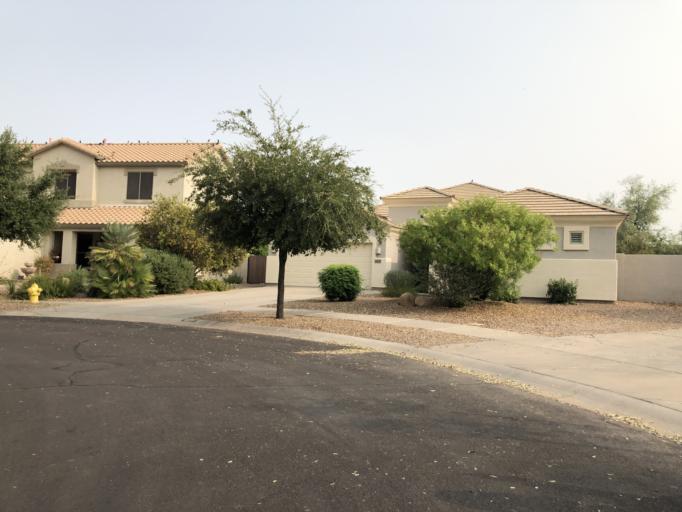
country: US
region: Arizona
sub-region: Maricopa County
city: Queen Creek
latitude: 33.2759
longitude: -111.6949
